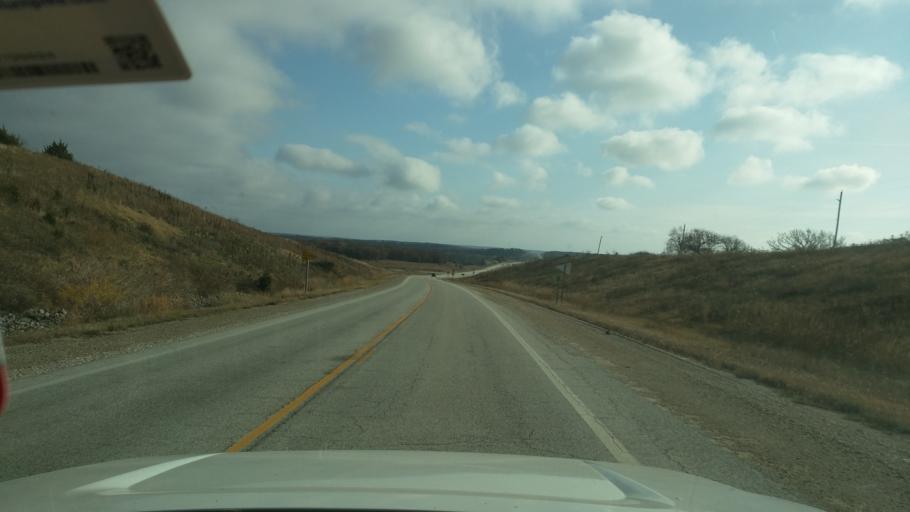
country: US
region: Kansas
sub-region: Chautauqua County
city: Sedan
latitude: 37.0834
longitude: -96.1879
